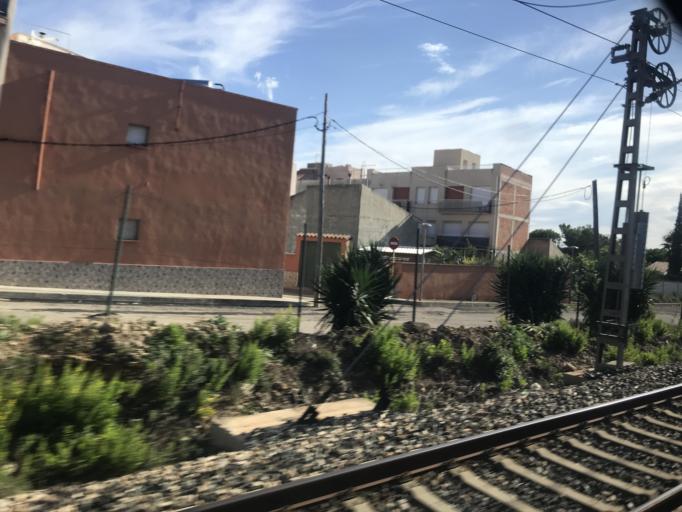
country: ES
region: Catalonia
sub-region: Provincia de Tarragona
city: L'Ampolla
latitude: 40.8088
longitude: 0.7032
